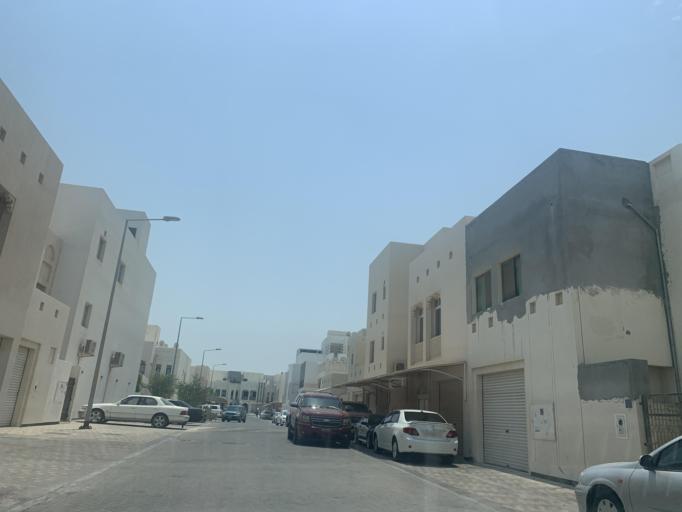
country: BH
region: Muharraq
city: Al Hadd
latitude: 26.2397
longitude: 50.6742
